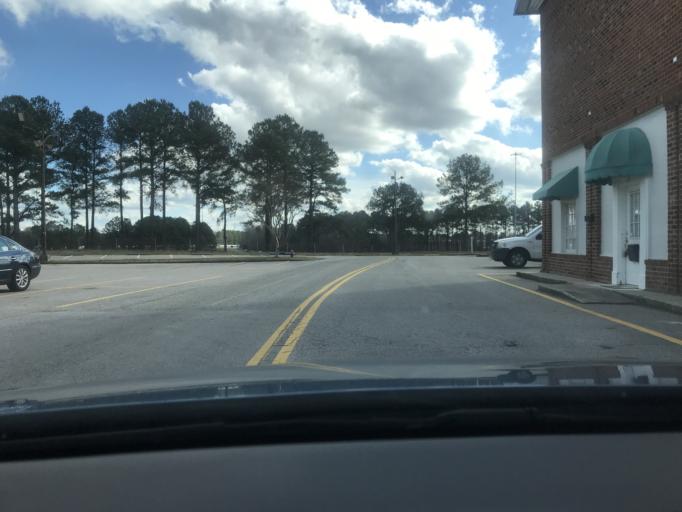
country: US
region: North Carolina
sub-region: Wake County
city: Cary
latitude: 35.7668
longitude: -78.7389
